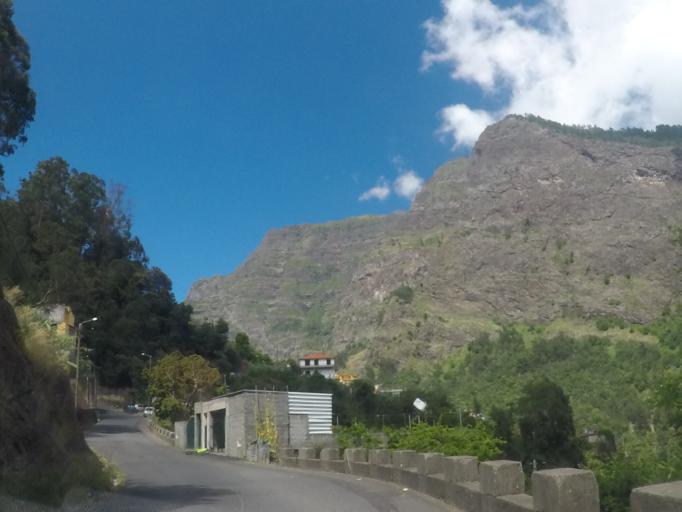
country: PT
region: Madeira
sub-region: Camara de Lobos
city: Curral das Freiras
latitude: 32.7069
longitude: -16.9754
